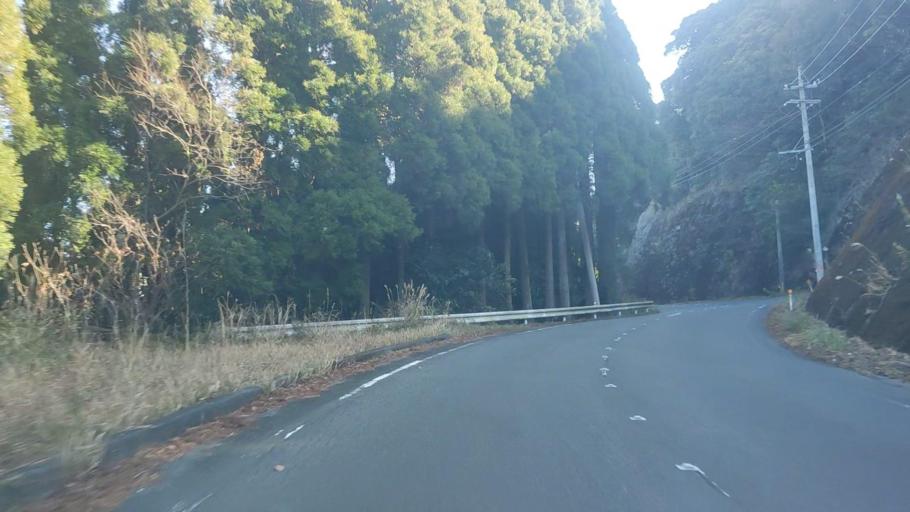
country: JP
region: Kagoshima
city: Kokubu-matsuki
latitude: 31.6711
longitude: 130.8320
